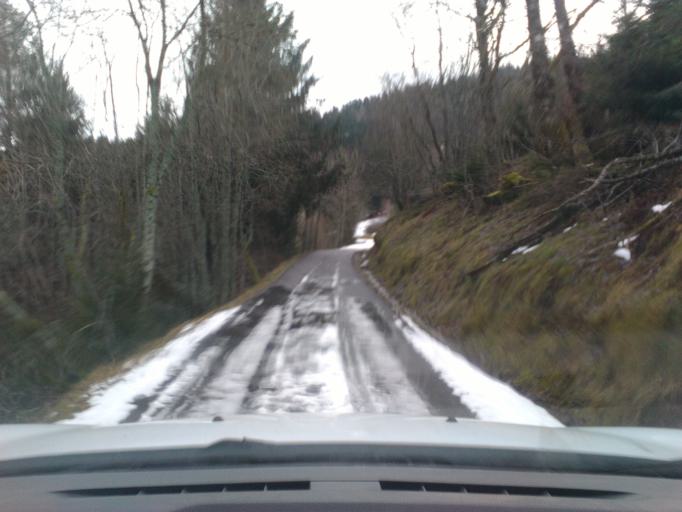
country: FR
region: Lorraine
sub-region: Departement des Vosges
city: La Bresse
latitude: 47.9970
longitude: 6.8921
